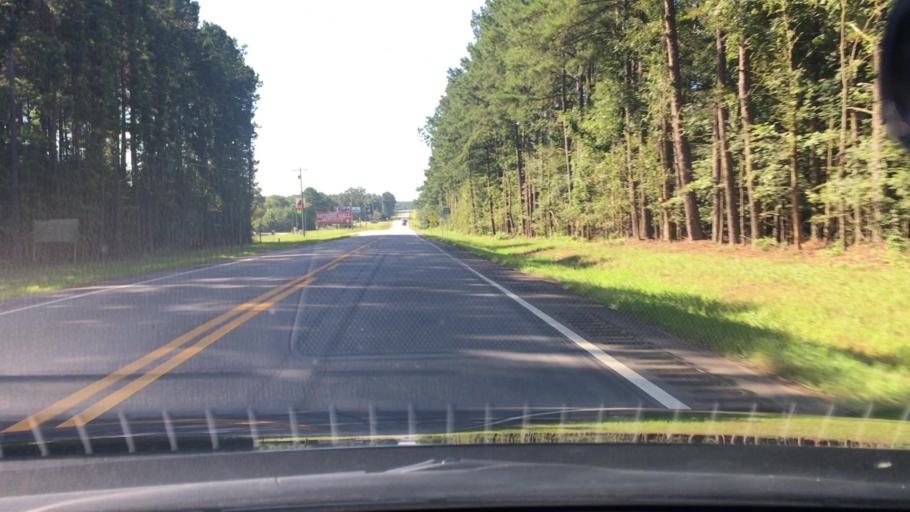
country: US
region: Georgia
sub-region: Putnam County
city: Jefferson
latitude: 33.4592
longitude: -83.4119
